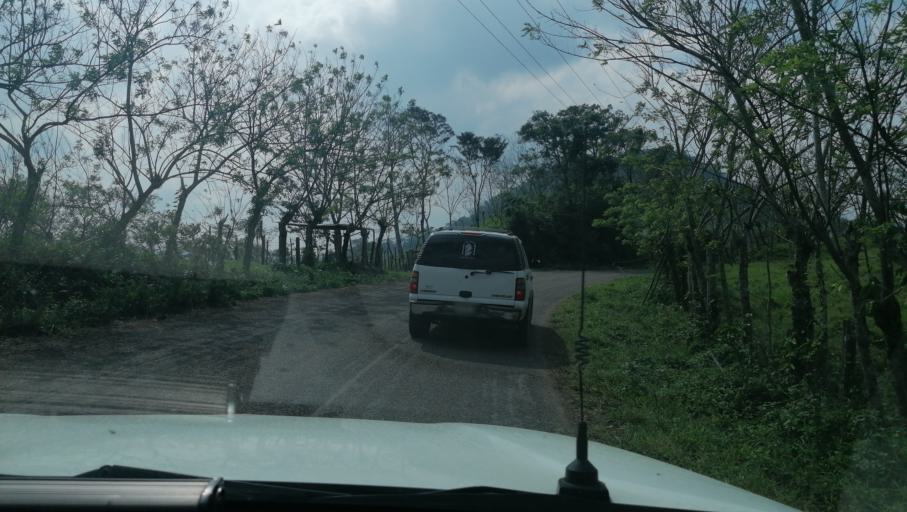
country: MX
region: Chiapas
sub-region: Francisco Leon
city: San Miguel la Sardina
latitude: 17.2288
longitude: -93.3477
